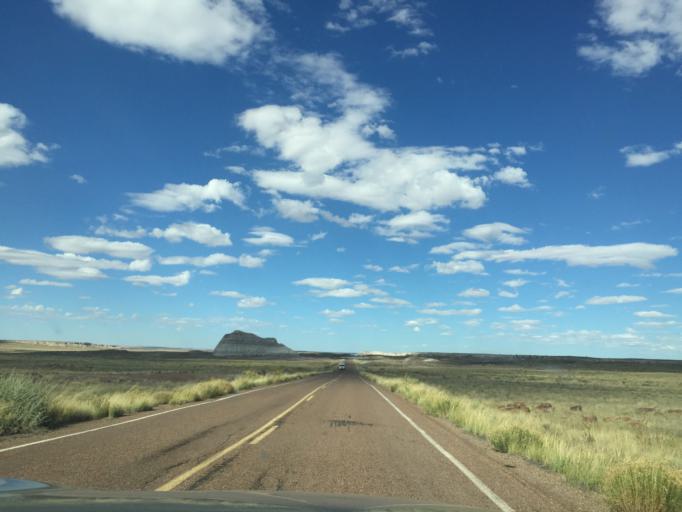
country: US
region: Arizona
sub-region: Navajo County
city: Holbrook
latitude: 34.8579
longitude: -109.7954
